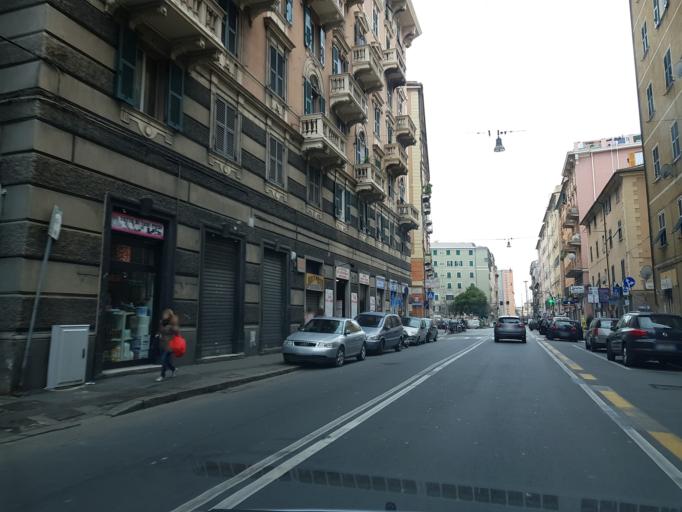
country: IT
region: Liguria
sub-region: Provincia di Genova
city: San Teodoro
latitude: 44.4194
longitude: 8.8868
